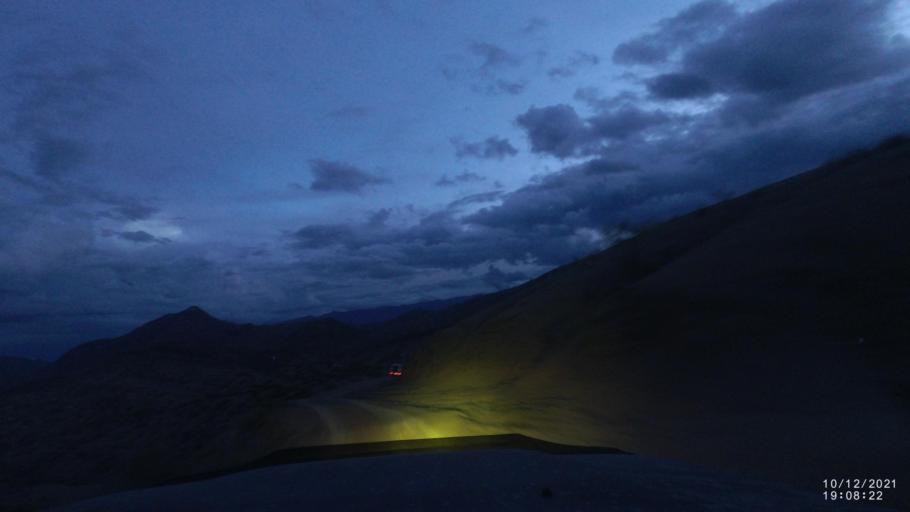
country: BO
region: Cochabamba
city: Tarata
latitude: -17.9105
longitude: -65.9369
